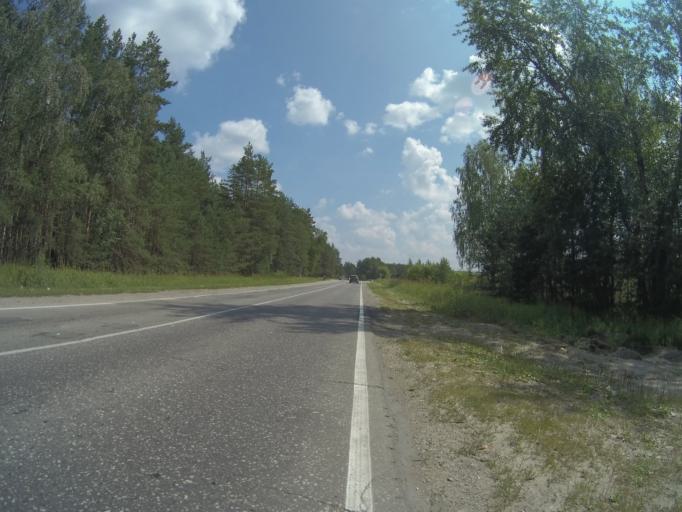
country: RU
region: Vladimir
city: Gus'-Khrustal'nyy
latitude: 55.6363
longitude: 40.7565
